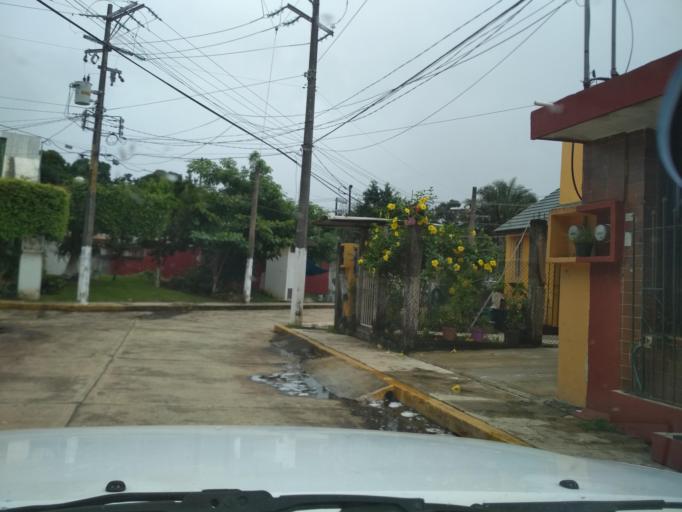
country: MX
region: Veracruz
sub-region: San Andres Tuxtla
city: Los Pinos
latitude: 18.4482
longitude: -95.2288
